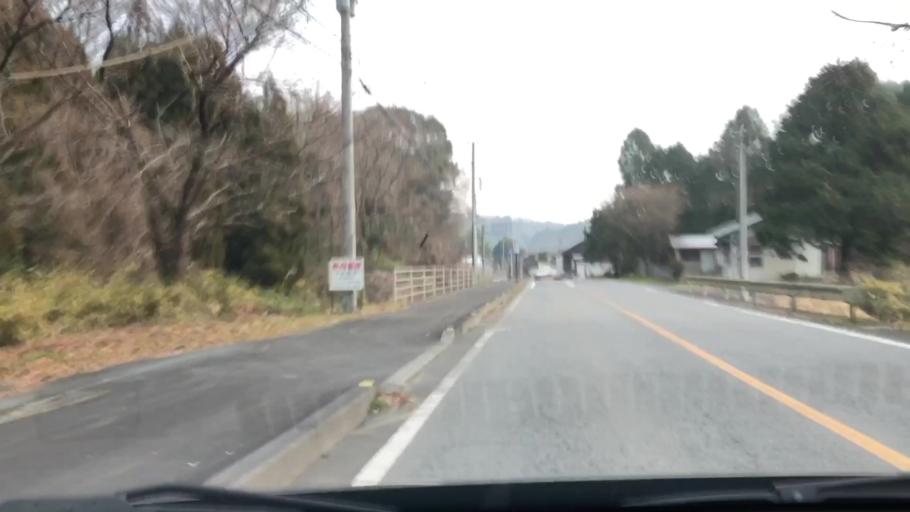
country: JP
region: Oita
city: Takedamachi
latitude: 32.9692
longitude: 131.5122
